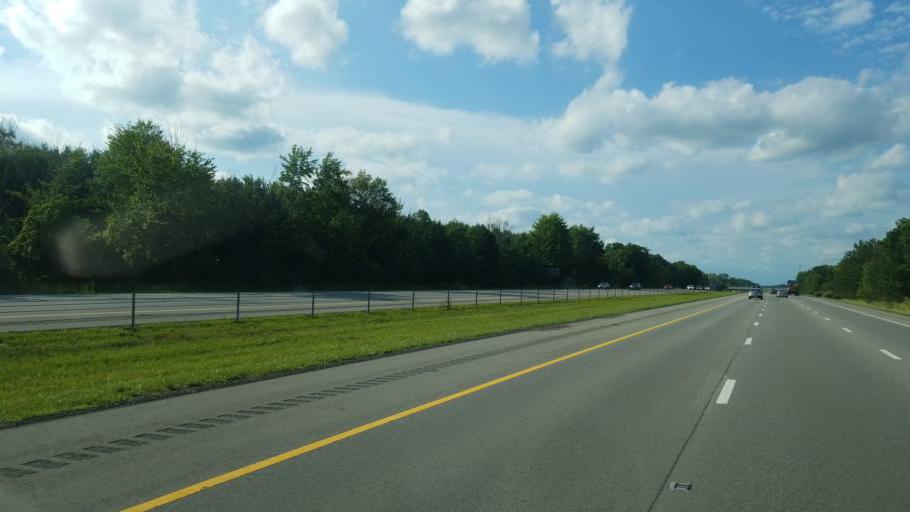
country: US
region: Ohio
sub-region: Morrow County
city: Cardington
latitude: 40.3920
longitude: -82.8232
